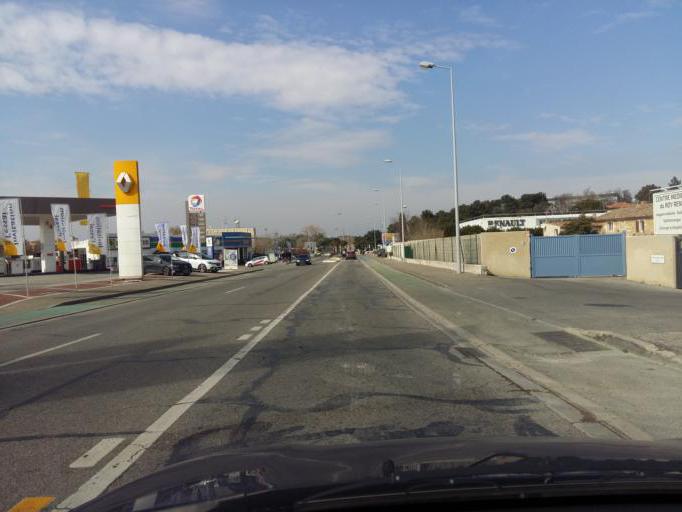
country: FR
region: Provence-Alpes-Cote d'Azur
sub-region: Departement des Bouches-du-Rhone
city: Salon-de-Provence
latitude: 43.6324
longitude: 5.0989
